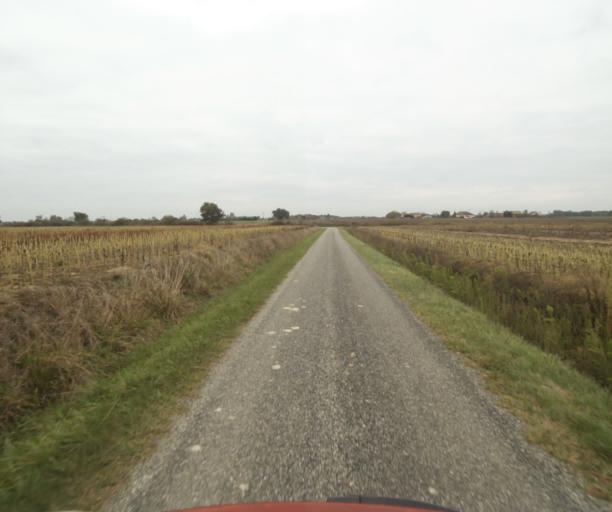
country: FR
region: Midi-Pyrenees
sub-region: Departement de la Haute-Garonne
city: Launac
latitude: 43.8022
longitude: 1.1930
